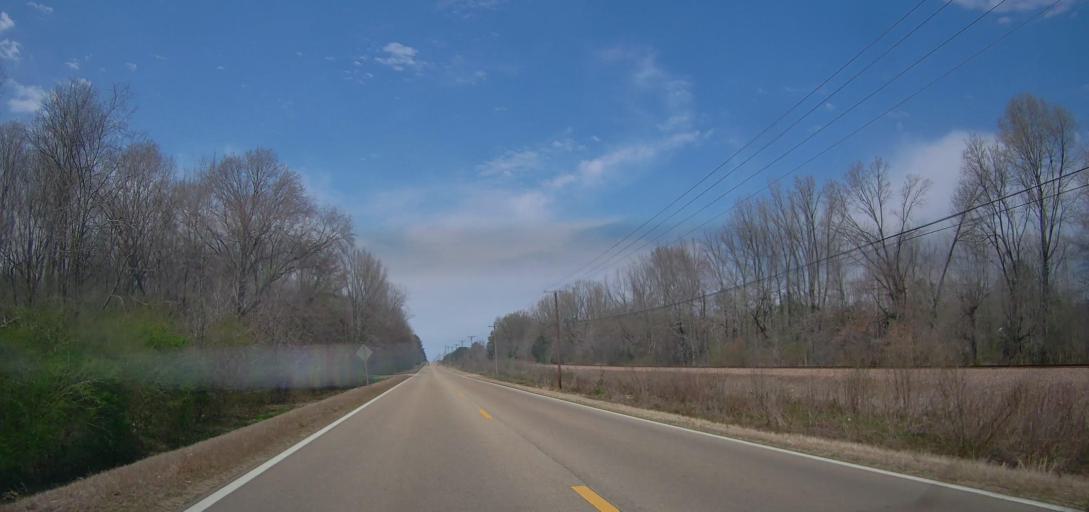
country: US
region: Mississippi
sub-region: Union County
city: New Albany
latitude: 34.5238
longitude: -89.0619
